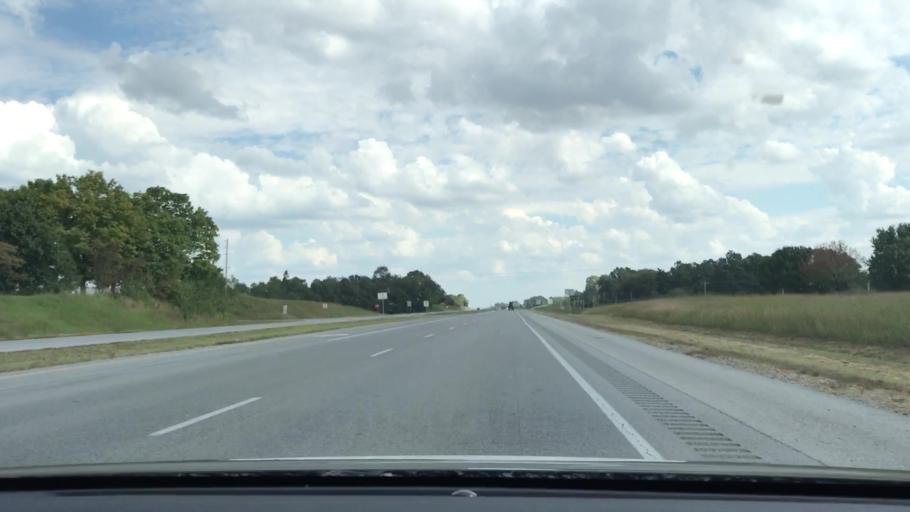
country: US
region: Kentucky
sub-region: Trigg County
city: Cadiz
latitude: 36.8683
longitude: -87.7757
